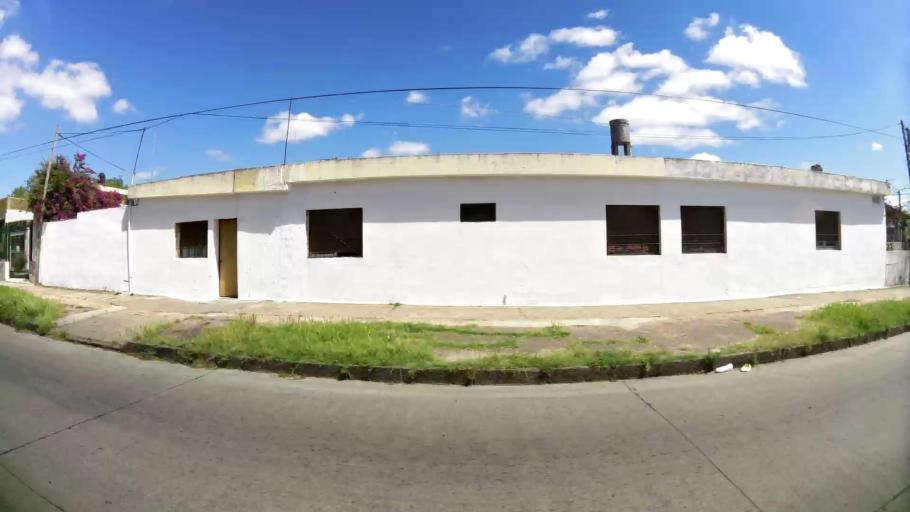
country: UY
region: Montevideo
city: Montevideo
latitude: -34.8524
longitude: -56.1375
